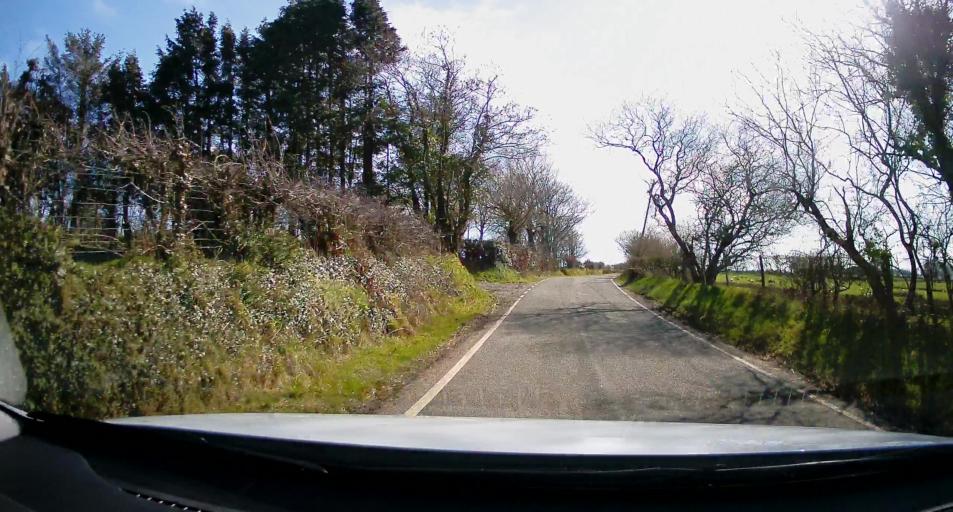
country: GB
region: Wales
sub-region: County of Ceredigion
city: Lledrod
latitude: 52.2908
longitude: -4.0656
